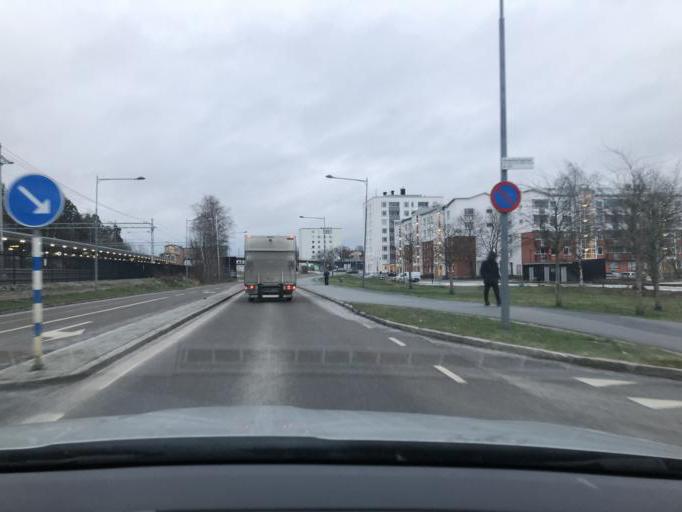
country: SE
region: Stockholm
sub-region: Stockholms Kommun
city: Kista
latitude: 59.3846
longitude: 17.8954
